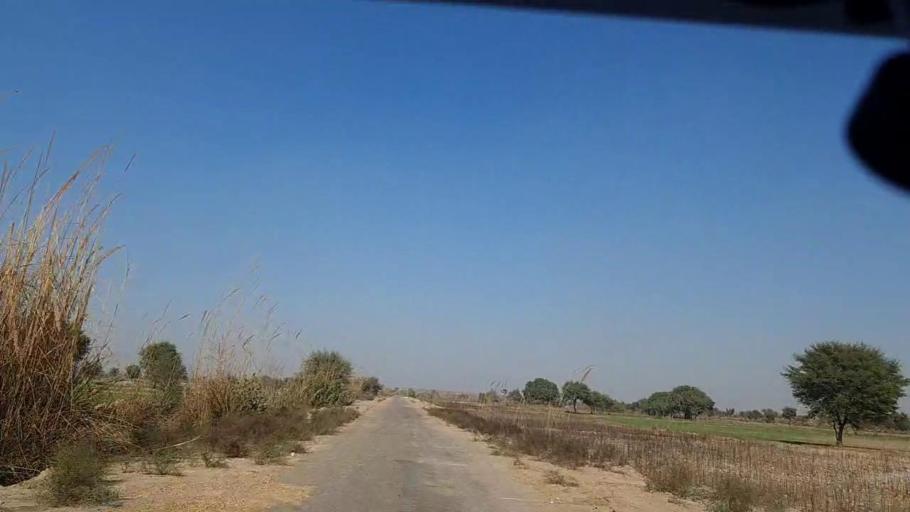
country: PK
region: Sindh
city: Khanpur
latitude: 27.5714
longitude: 69.3797
